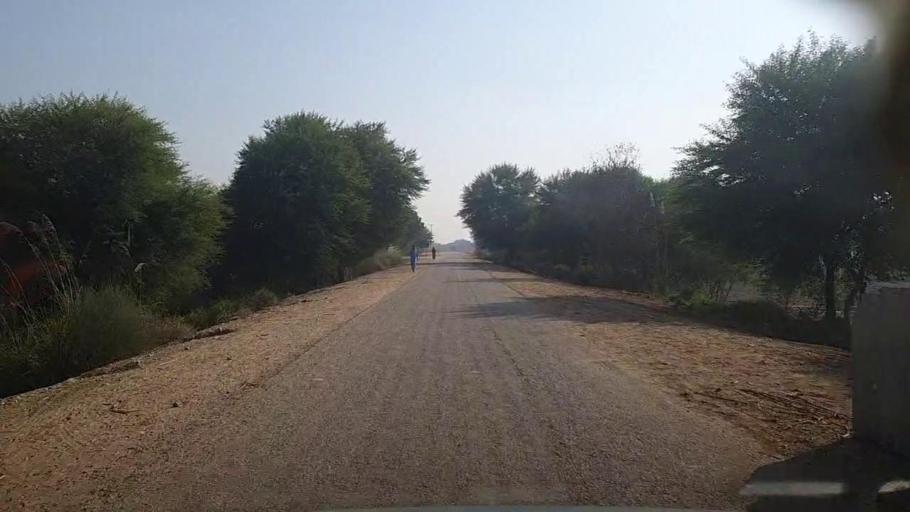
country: PK
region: Sindh
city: Kandiari
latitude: 26.8370
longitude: 68.4892
